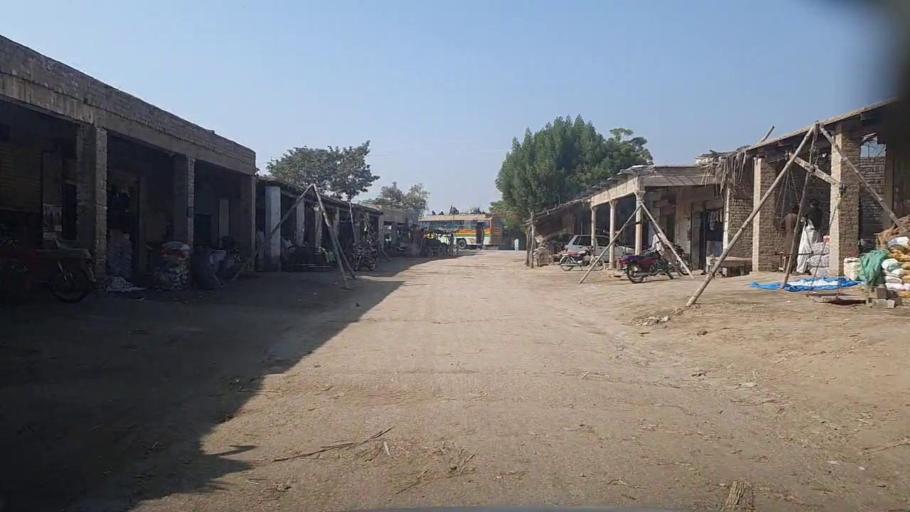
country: PK
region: Sindh
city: Karaundi
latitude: 26.9797
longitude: 68.4461
